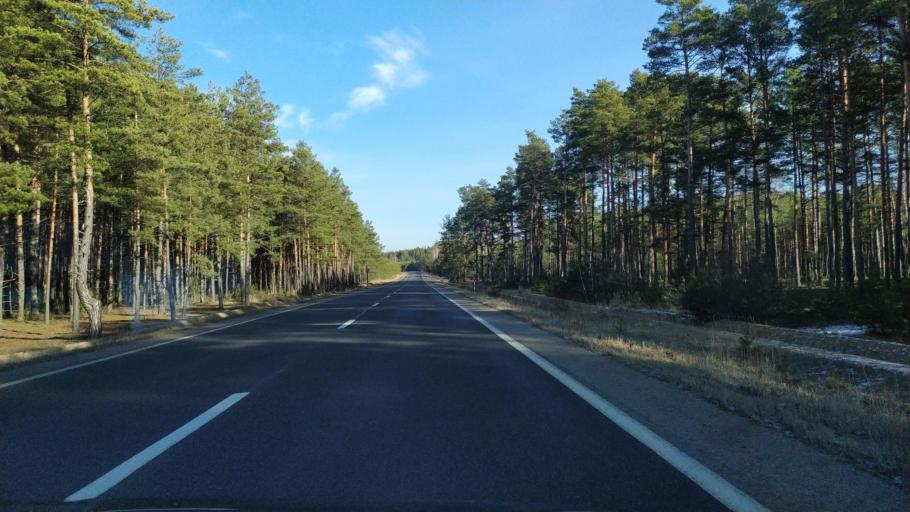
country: BY
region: Brest
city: Zhabinka
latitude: 52.4423
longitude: 24.1327
